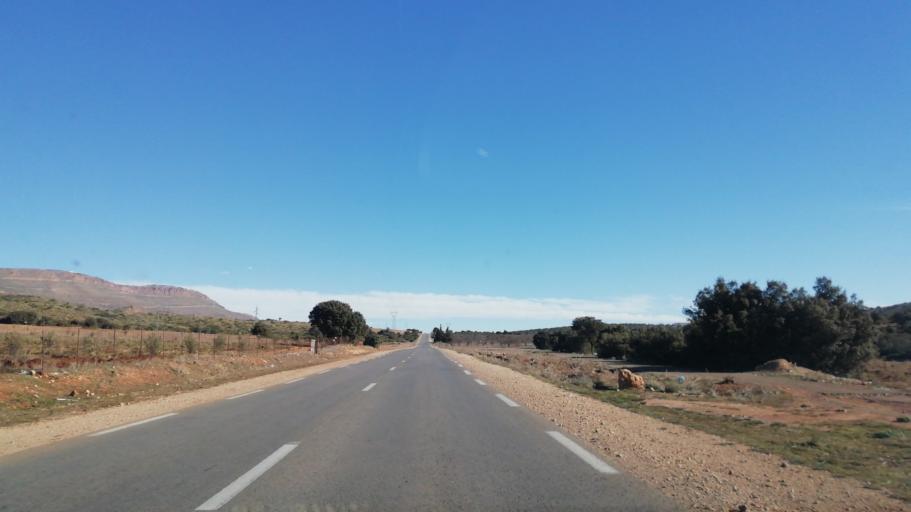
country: DZ
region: Tlemcen
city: Sebdou
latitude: 34.7078
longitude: -1.2148
